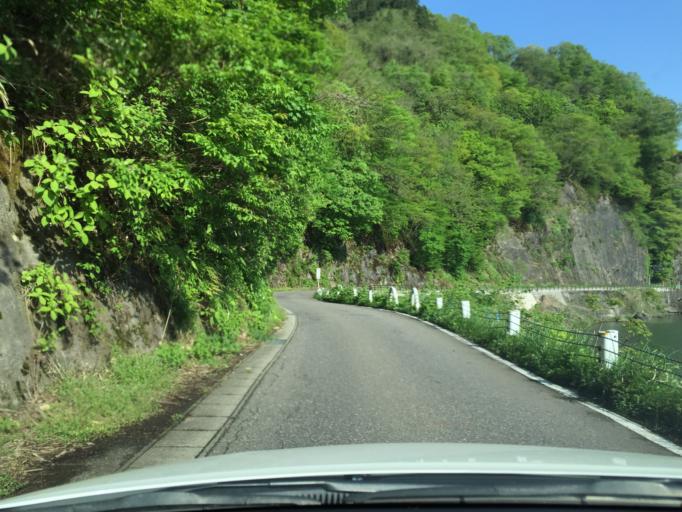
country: JP
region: Fukushima
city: Kitakata
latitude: 37.6651
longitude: 139.5915
